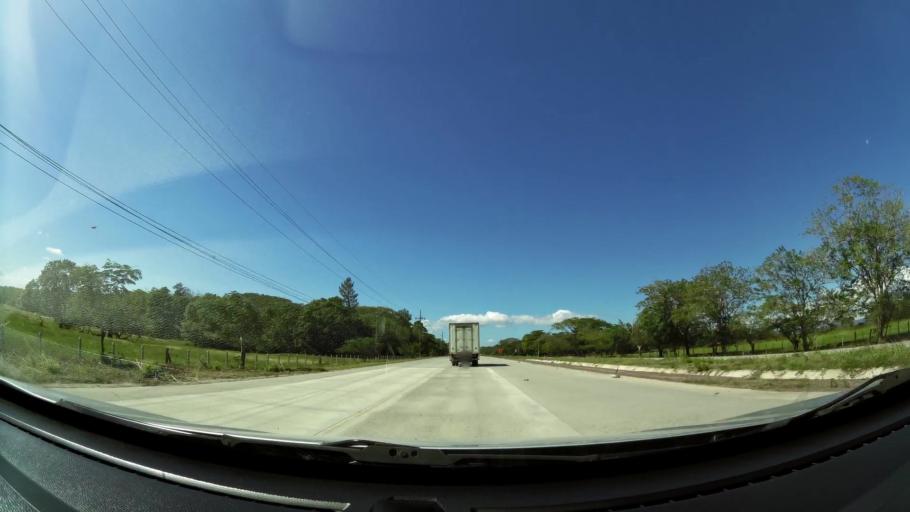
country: CR
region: Guanacaste
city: Liberia
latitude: 10.5747
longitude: -85.3999
